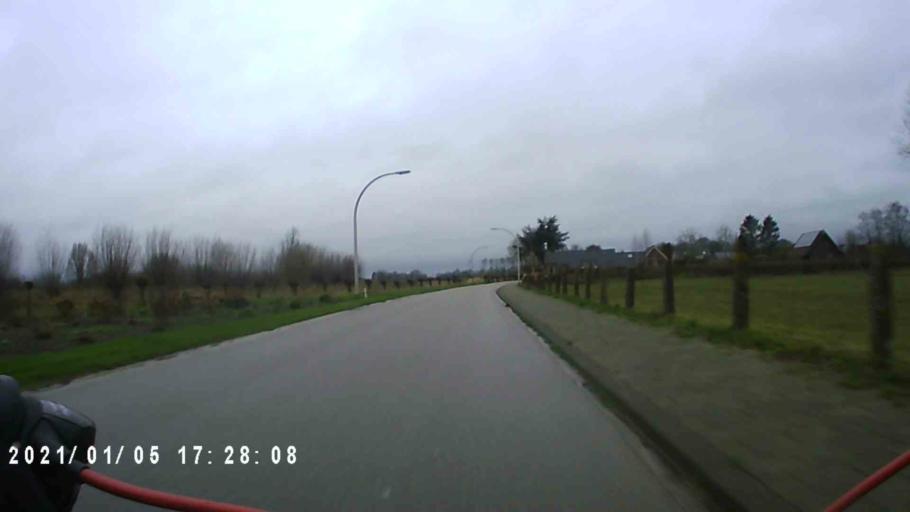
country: NL
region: Groningen
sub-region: Gemeente Delfzijl
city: Delfzijl
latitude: 53.2231
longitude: 6.9482
